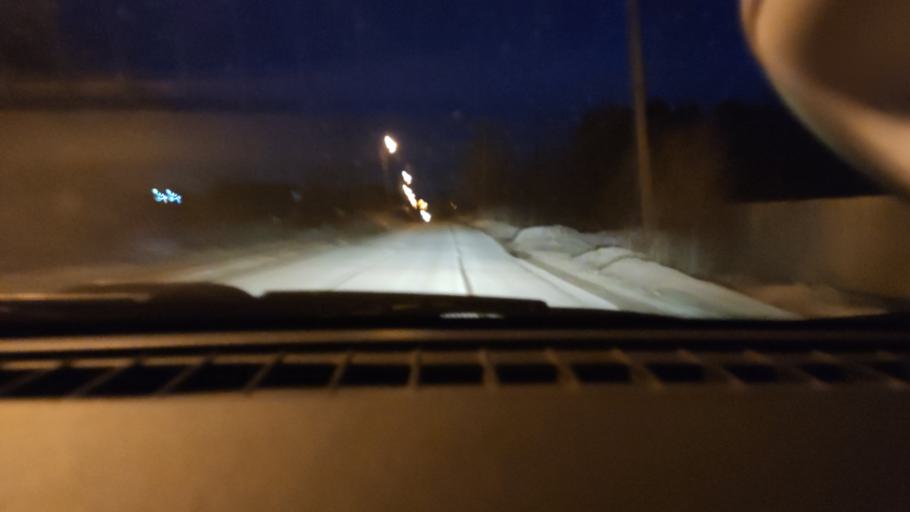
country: RU
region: Perm
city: Overyata
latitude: 58.0905
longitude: 55.8588
